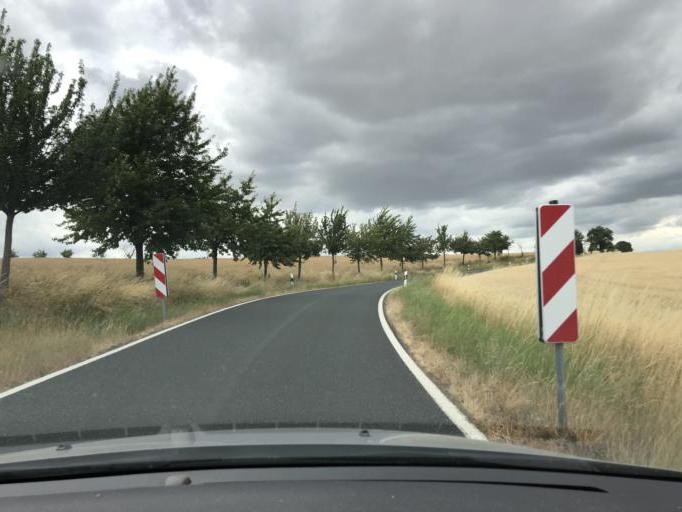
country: DE
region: Saxony
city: Geithain
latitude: 51.0191
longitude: 12.6493
